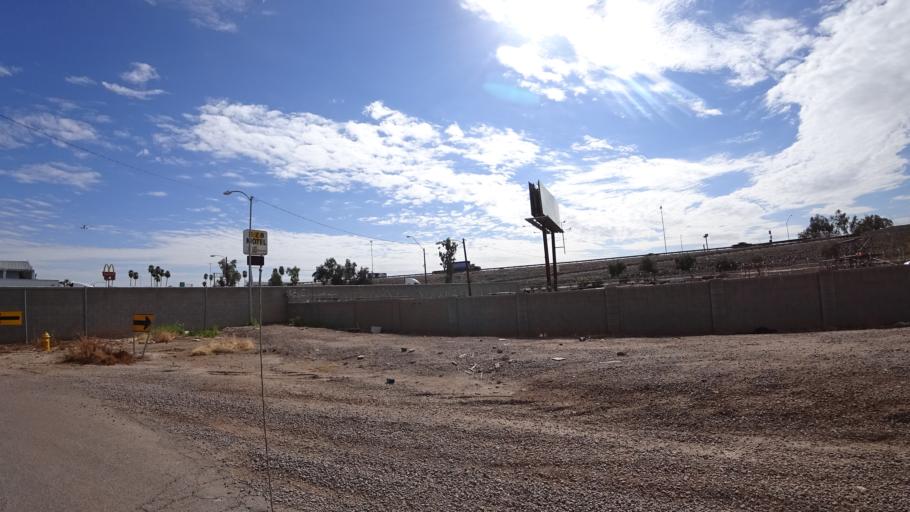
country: US
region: Arizona
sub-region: Maricopa County
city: Phoenix
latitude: 33.4295
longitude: -112.0677
